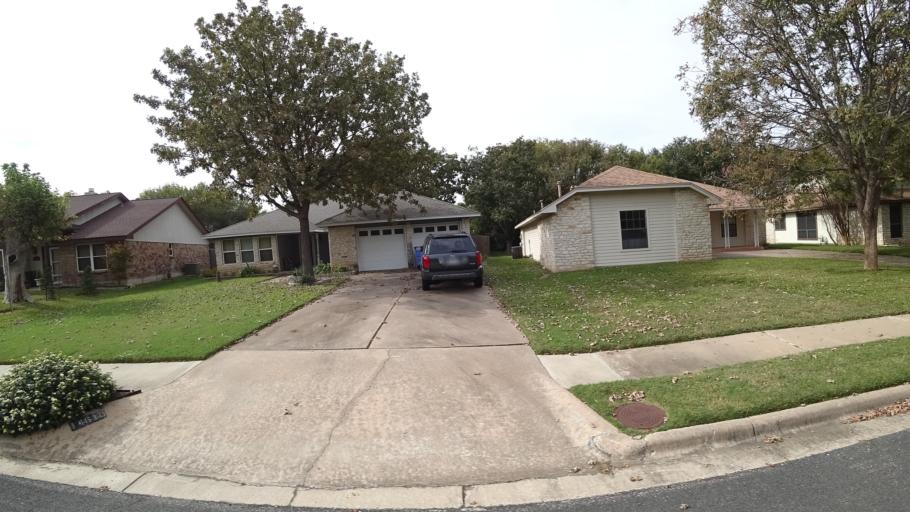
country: US
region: Texas
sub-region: Travis County
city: Wells Branch
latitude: 30.4437
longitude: -97.6828
